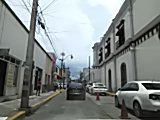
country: MX
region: Nayarit
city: Tepic
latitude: 21.5071
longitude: -104.8940
